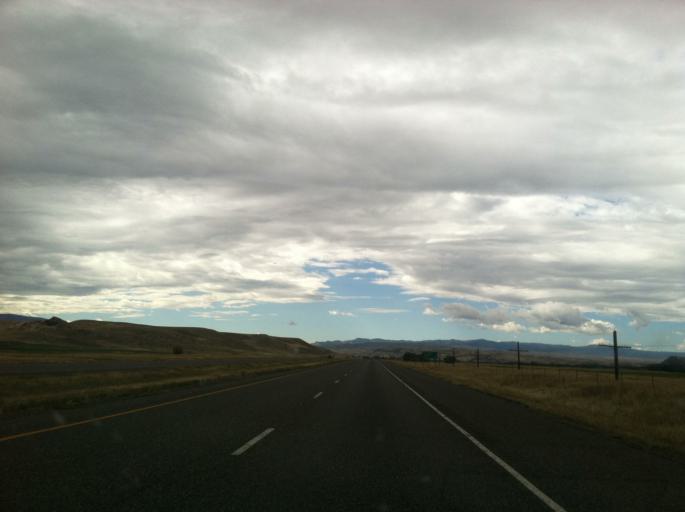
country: US
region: Montana
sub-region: Park County
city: Livingston
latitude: 45.7134
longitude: -110.4155
